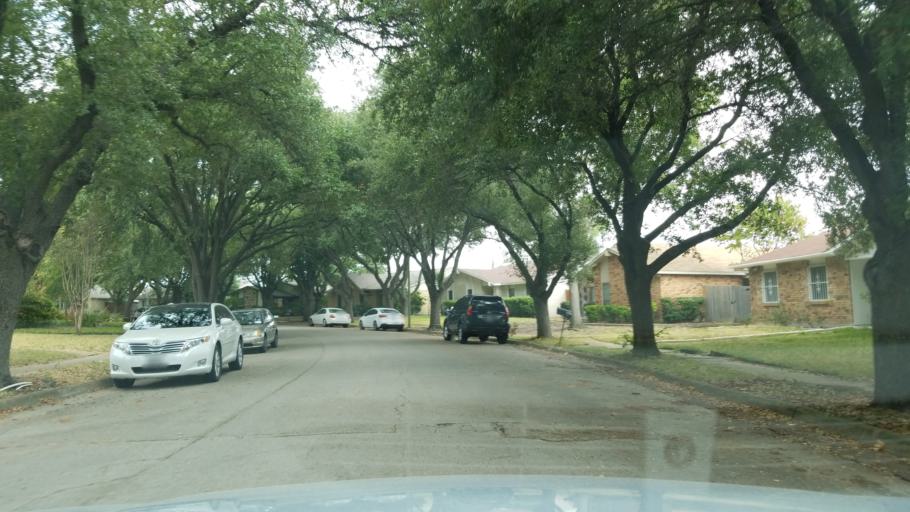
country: US
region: Texas
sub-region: Dallas County
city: Garland
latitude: 32.8760
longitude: -96.6931
